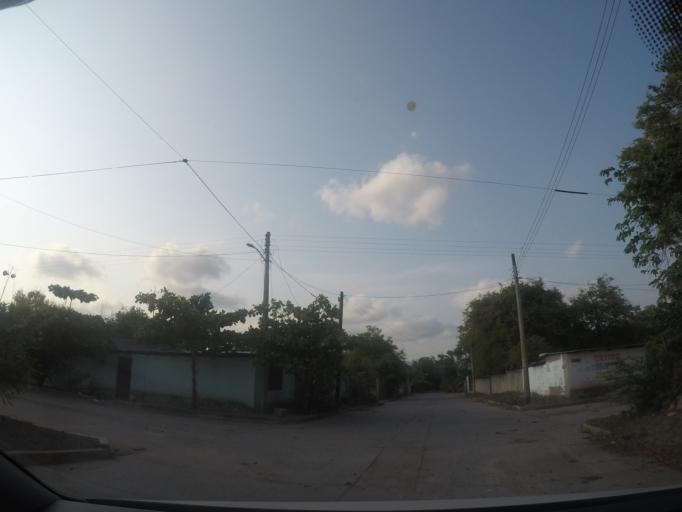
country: MX
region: Oaxaca
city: San Jeronimo Ixtepec
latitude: 16.5916
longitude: -95.1588
